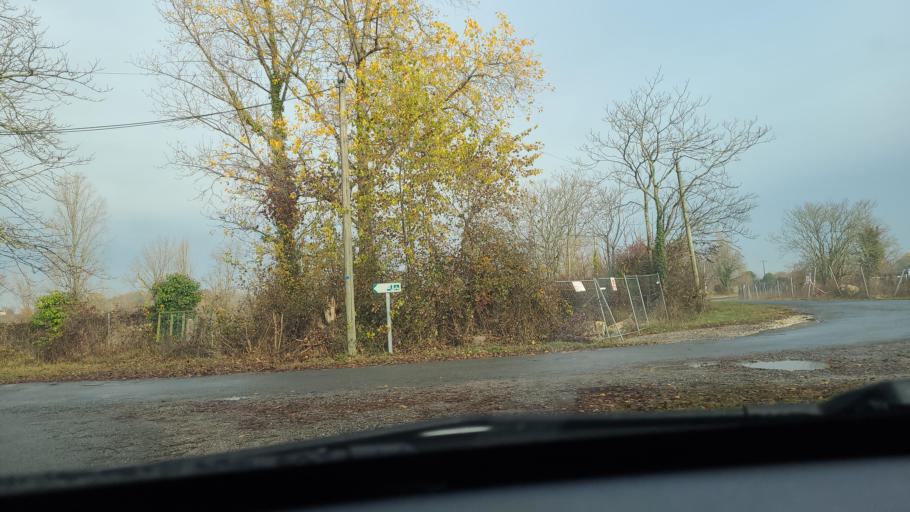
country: FR
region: Aquitaine
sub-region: Departement de la Gironde
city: Marcamps
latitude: 45.0315
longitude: -0.4781
